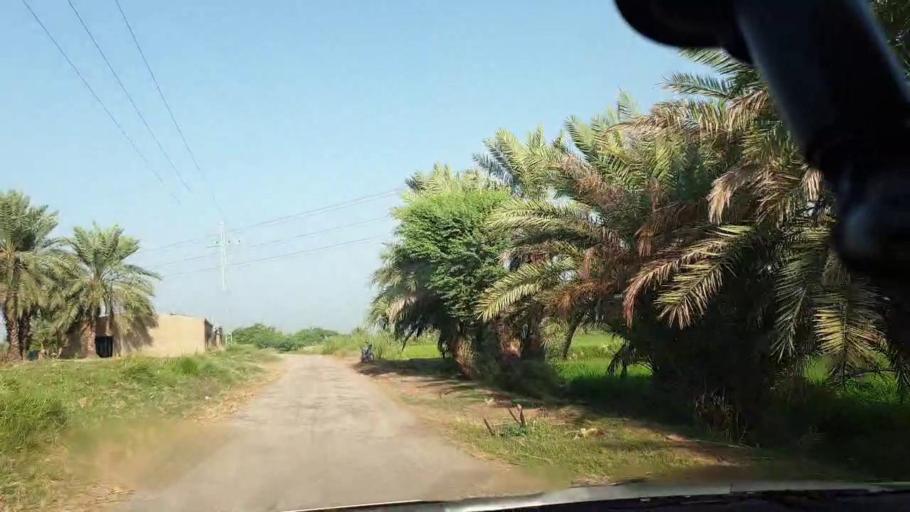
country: PK
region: Sindh
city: Larkana
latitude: 27.6207
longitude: 68.2079
